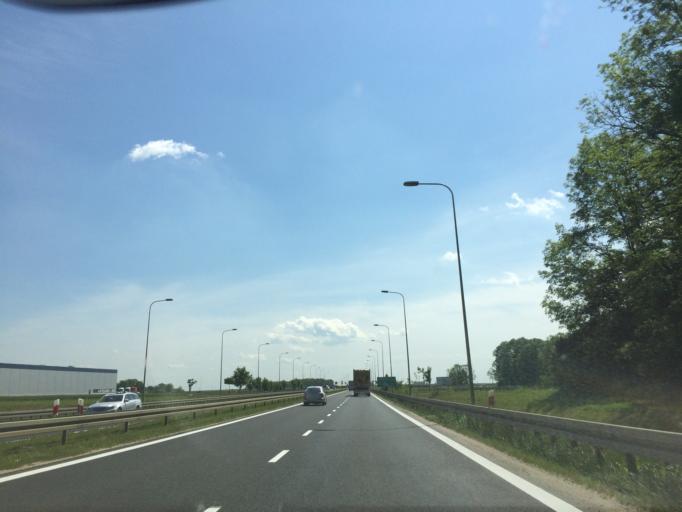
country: PL
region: Lower Silesian Voivodeship
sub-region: Powiat wroclawski
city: Tyniec Maly
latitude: 51.0326
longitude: 16.9273
